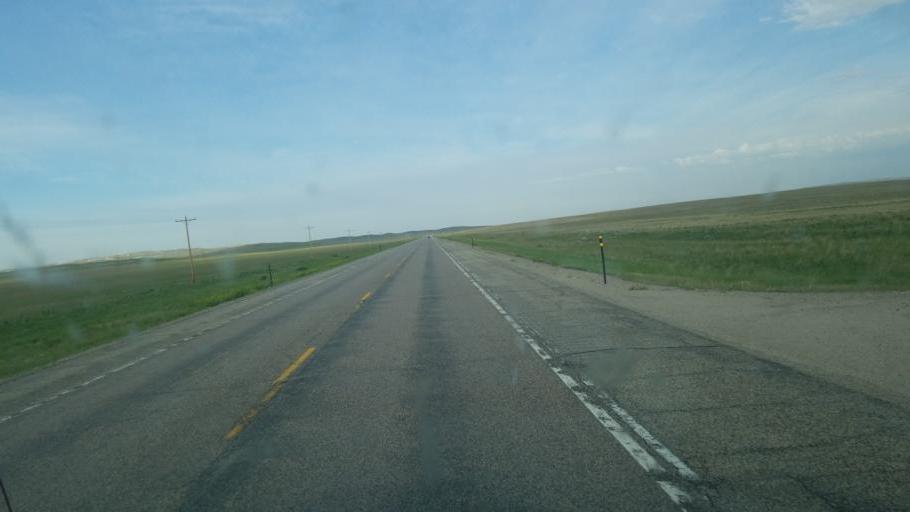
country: US
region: Wyoming
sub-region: Natrona County
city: Mills
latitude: 43.0282
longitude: -106.9287
